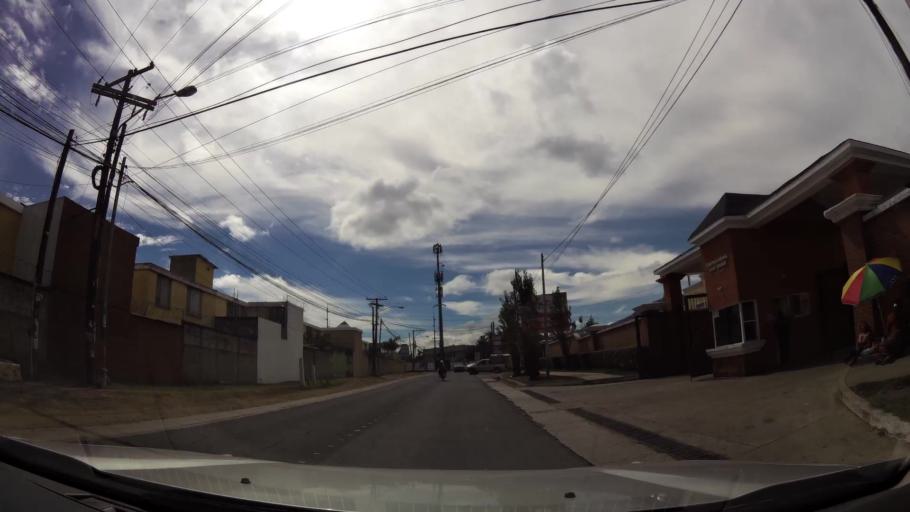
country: GT
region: Guatemala
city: Mixco
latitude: 14.6371
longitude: -90.5876
